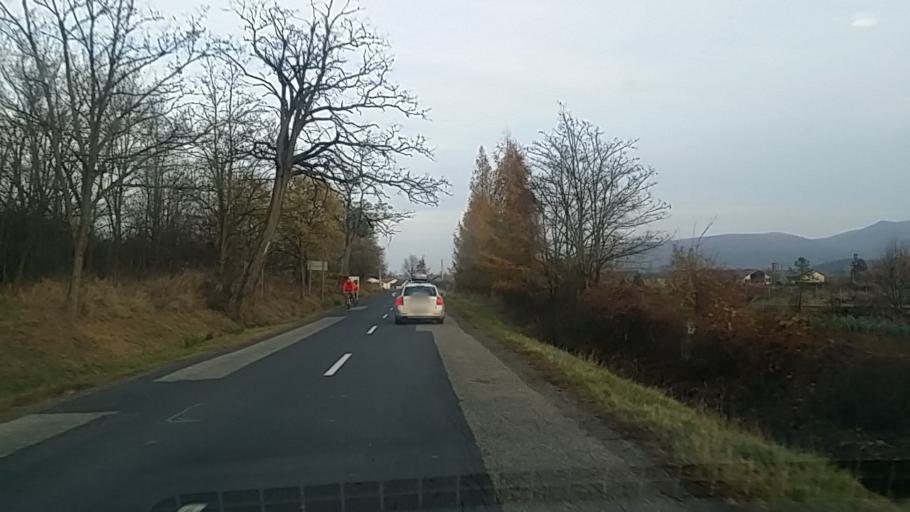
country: HU
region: Borsod-Abauj-Zemplen
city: Sarospatak
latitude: 48.4695
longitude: 21.5007
